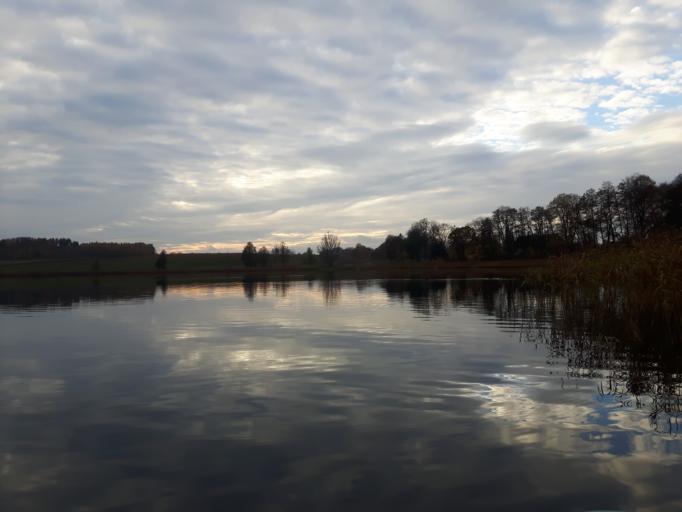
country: PL
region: Warmian-Masurian Voivodeship
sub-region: Powiat olsztynski
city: Barczewo
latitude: 53.8287
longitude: 20.7343
